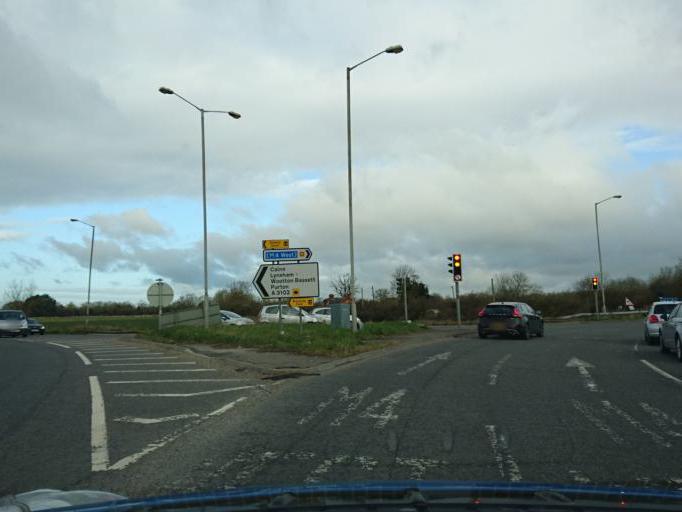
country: GB
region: England
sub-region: Wiltshire
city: Lydiard Tregoze
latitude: 51.5443
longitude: -1.8548
